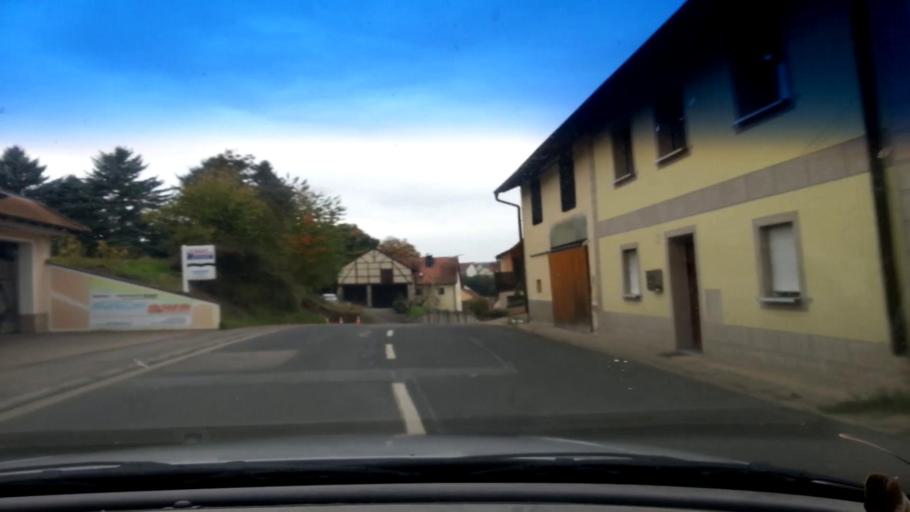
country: DE
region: Bavaria
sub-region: Upper Franconia
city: Priesendorf
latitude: 49.9044
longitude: 10.6768
